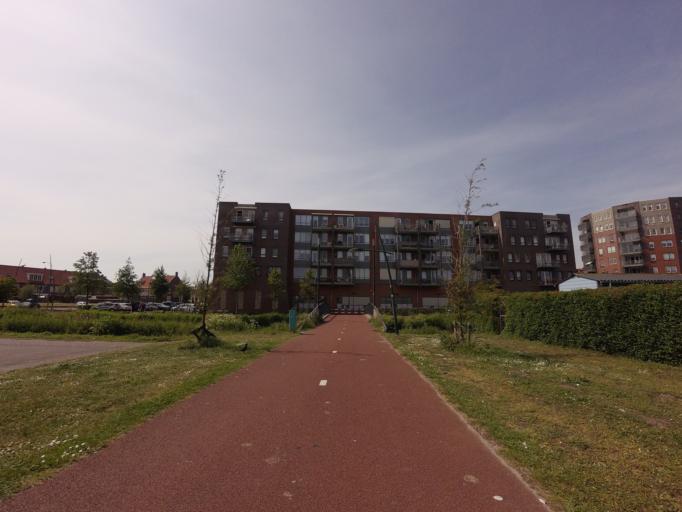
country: NL
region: North Holland
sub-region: Gemeente Uitgeest
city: Uitgeest
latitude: 52.4876
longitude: 4.7532
